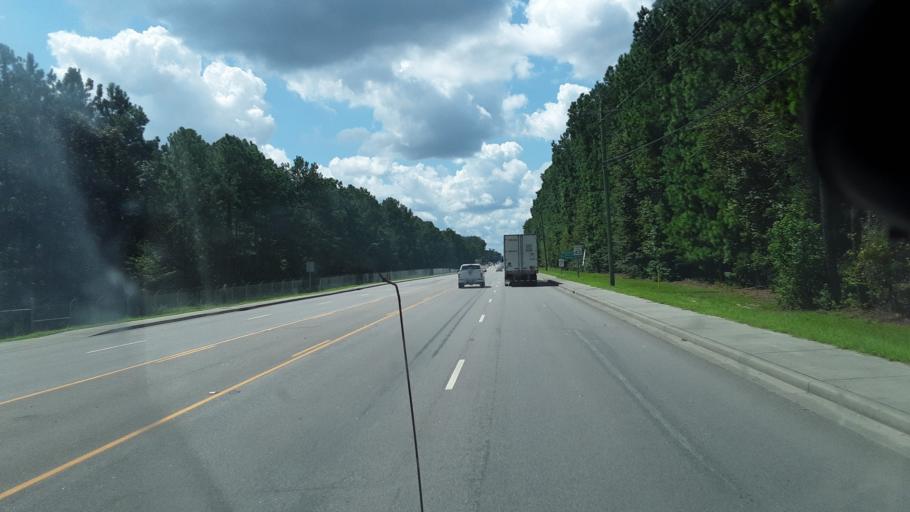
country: US
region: South Carolina
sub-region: Berkeley County
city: Sangaree
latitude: 33.0677
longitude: -80.0901
